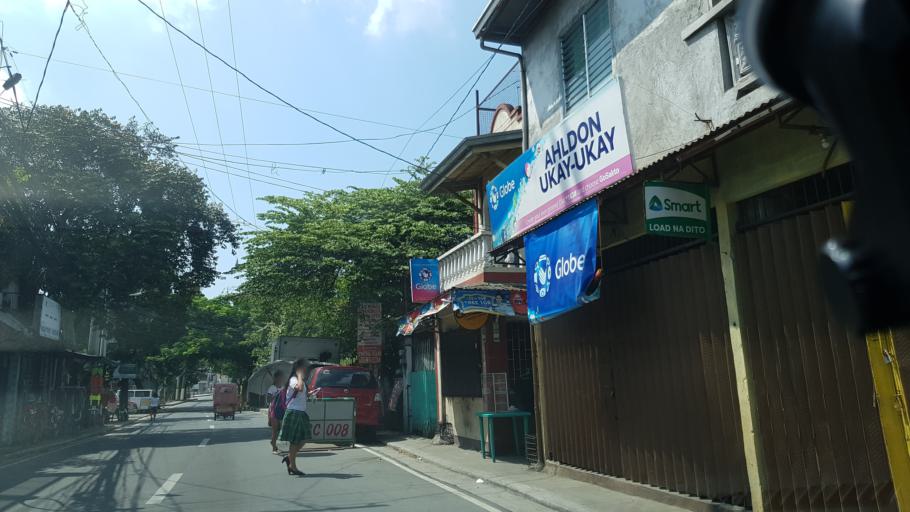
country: PH
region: Calabarzon
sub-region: Province of Rizal
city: Las Pinas
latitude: 14.4646
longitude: 120.9857
